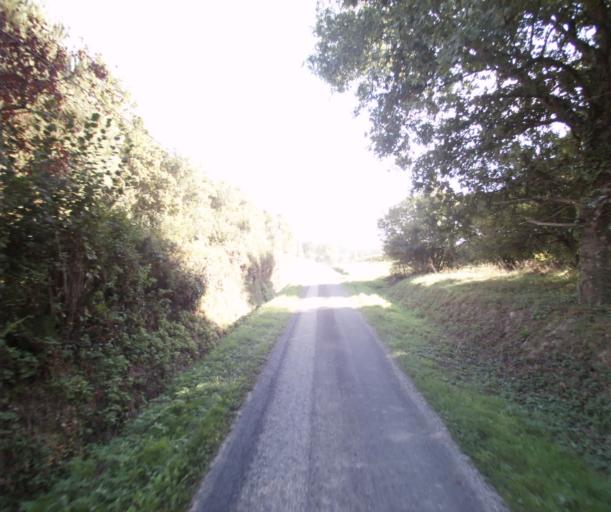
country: FR
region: Midi-Pyrenees
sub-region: Departement du Gers
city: Eauze
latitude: 43.8595
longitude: 0.0317
